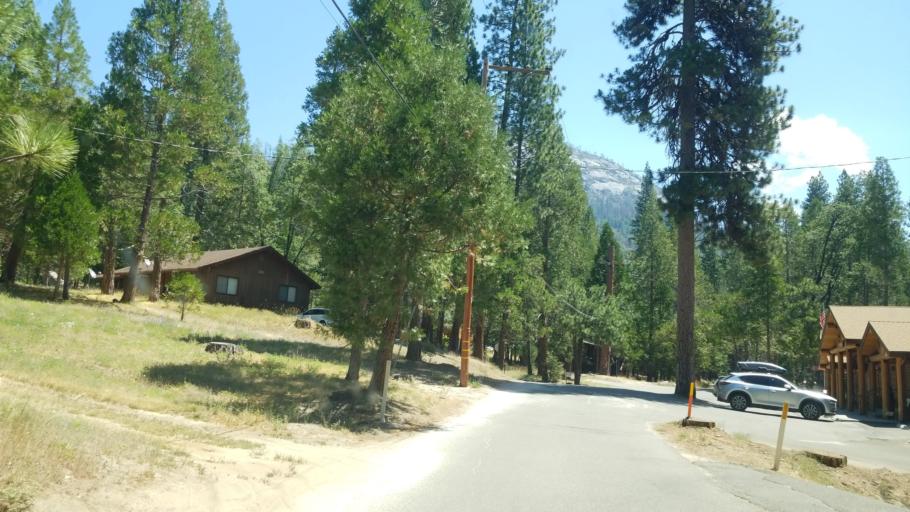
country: US
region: California
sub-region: Mariposa County
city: Yosemite Valley
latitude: 37.5488
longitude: -119.6409
